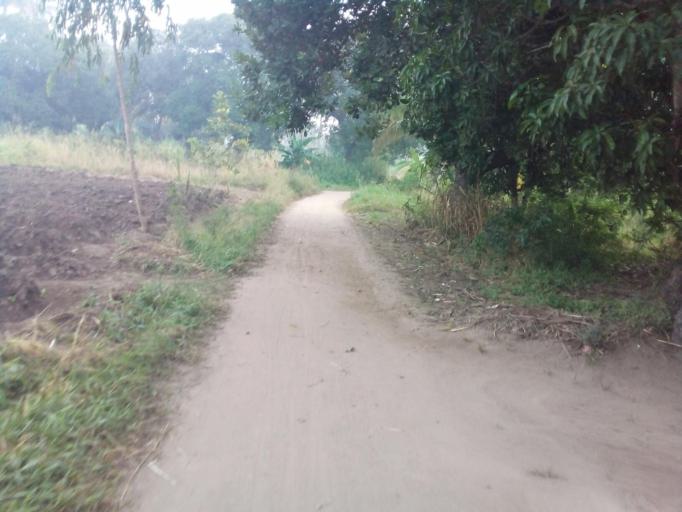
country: MZ
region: Zambezia
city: Quelimane
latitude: -17.5887
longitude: 36.6846
